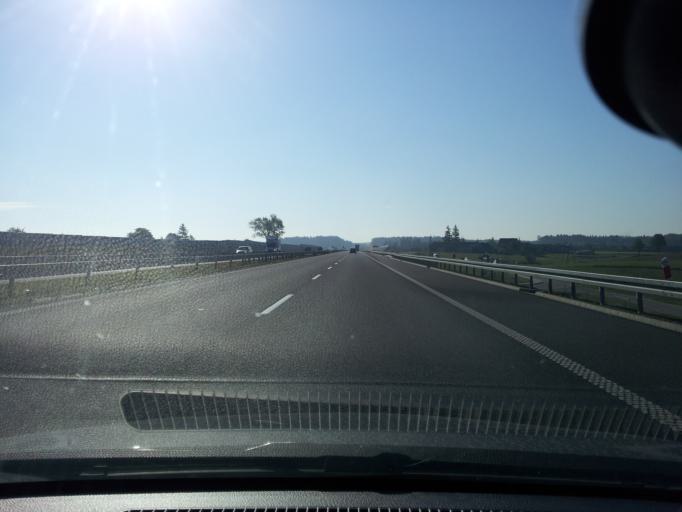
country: PL
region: Pomeranian Voivodeship
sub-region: Powiat starogardzki
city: Smetowo Graniczne
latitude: 53.6848
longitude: 18.6320
